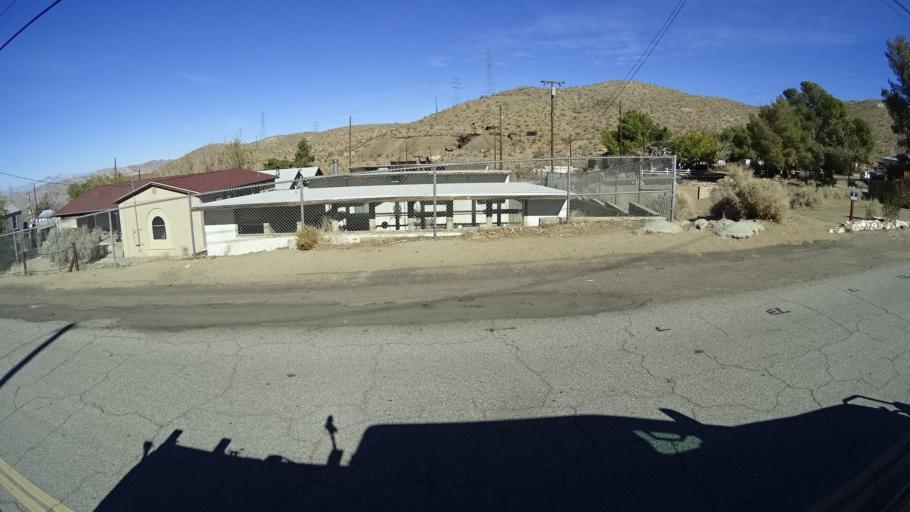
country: US
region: California
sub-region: Kern County
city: Ridgecrest
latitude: 35.3682
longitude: -117.6519
